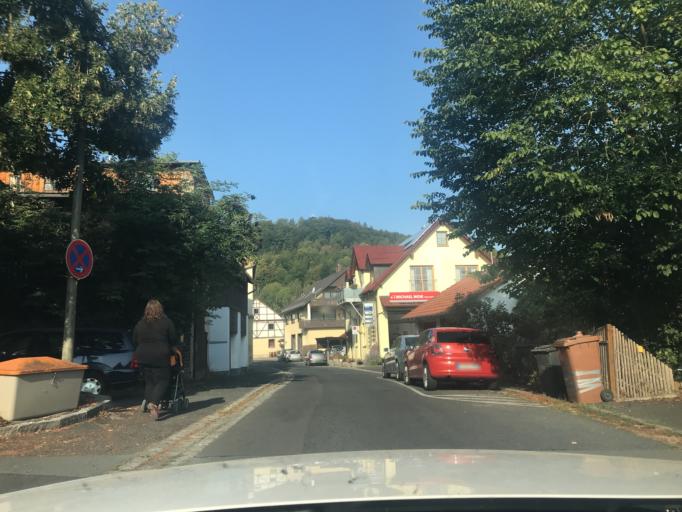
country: DE
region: Bavaria
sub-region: Upper Franconia
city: Pegnitz
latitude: 49.7571
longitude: 11.5411
